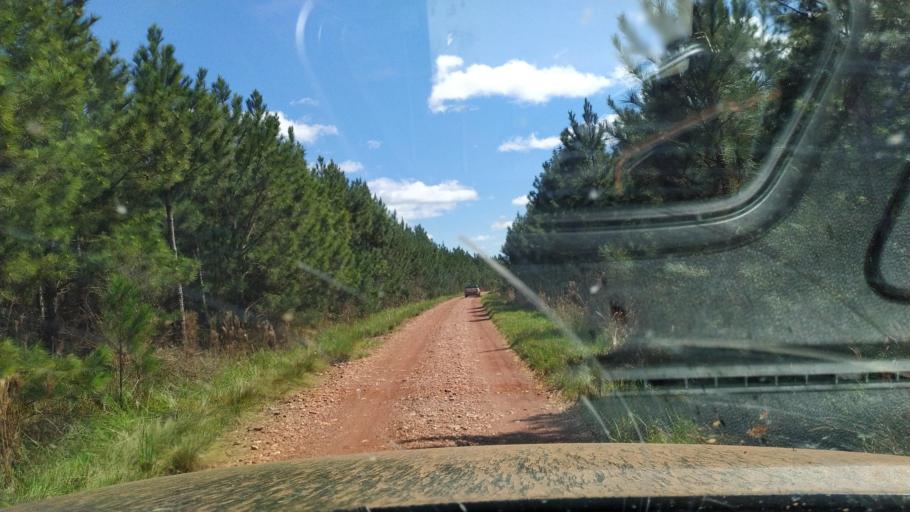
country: AR
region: Corrientes
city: Santo Tome
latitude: -28.4629
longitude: -55.9826
